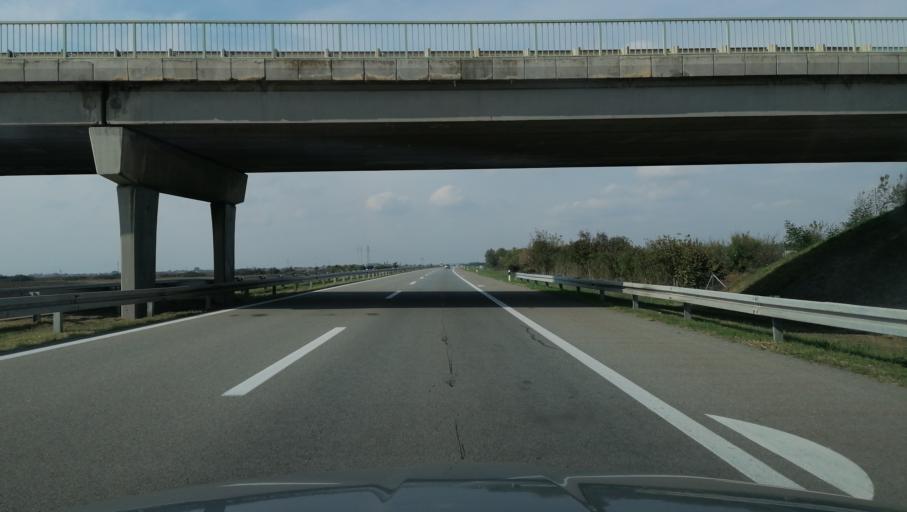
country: RS
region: Autonomna Pokrajina Vojvodina
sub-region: Sremski Okrug
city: Sremska Mitrovica
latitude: 45.0035
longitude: 19.6119
